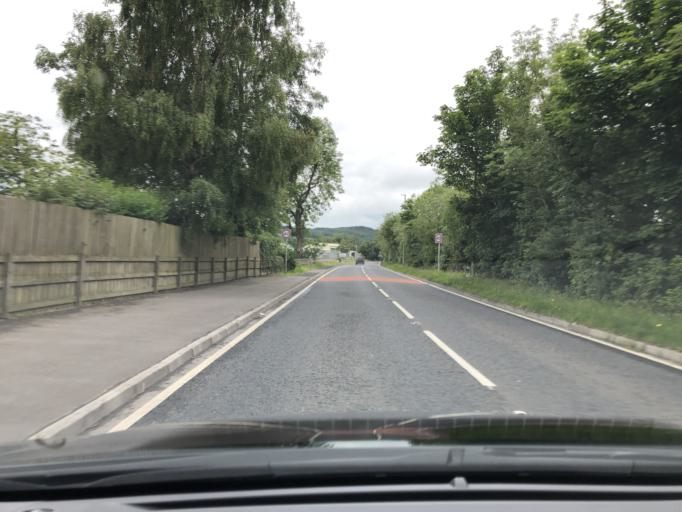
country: GB
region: Northern Ireland
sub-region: Down District
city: Castlewellan
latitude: 54.2555
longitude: -5.9526
